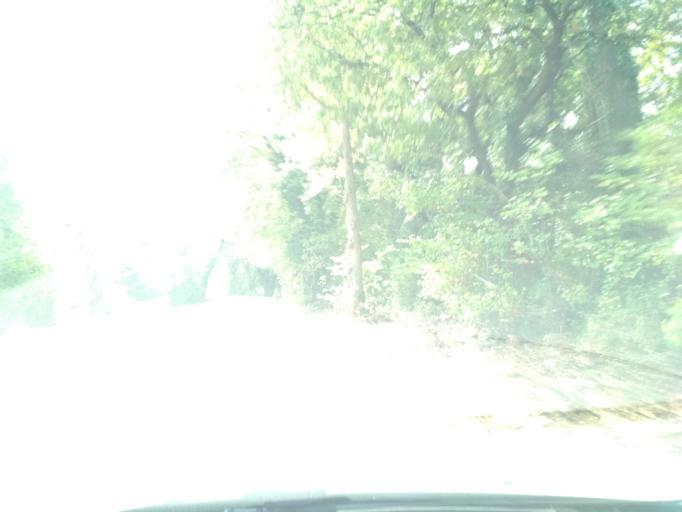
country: GR
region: Central Greece
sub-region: Nomos Evvoias
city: Prokopion
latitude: 38.7277
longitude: 23.5031
